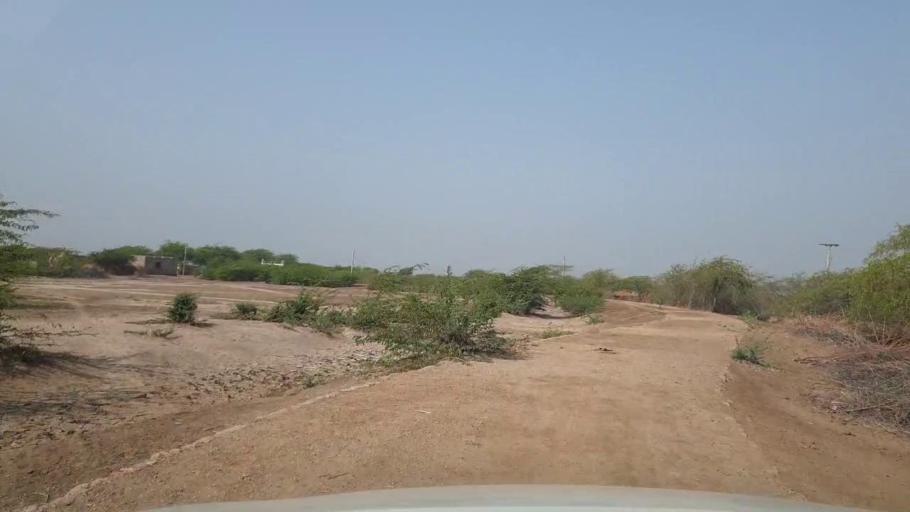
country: PK
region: Sindh
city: Chor
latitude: 25.4747
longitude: 69.7075
